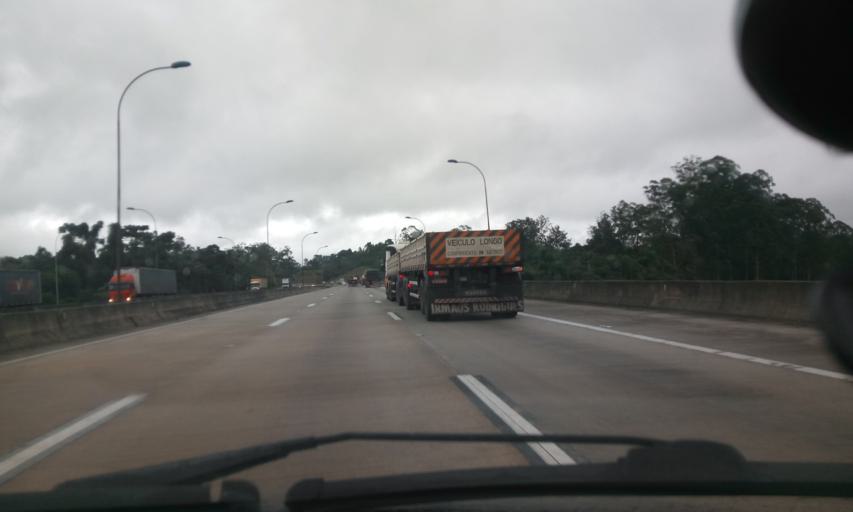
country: BR
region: Sao Paulo
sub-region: Embu-Guacu
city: Embu Guacu
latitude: -23.7641
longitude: -46.7709
